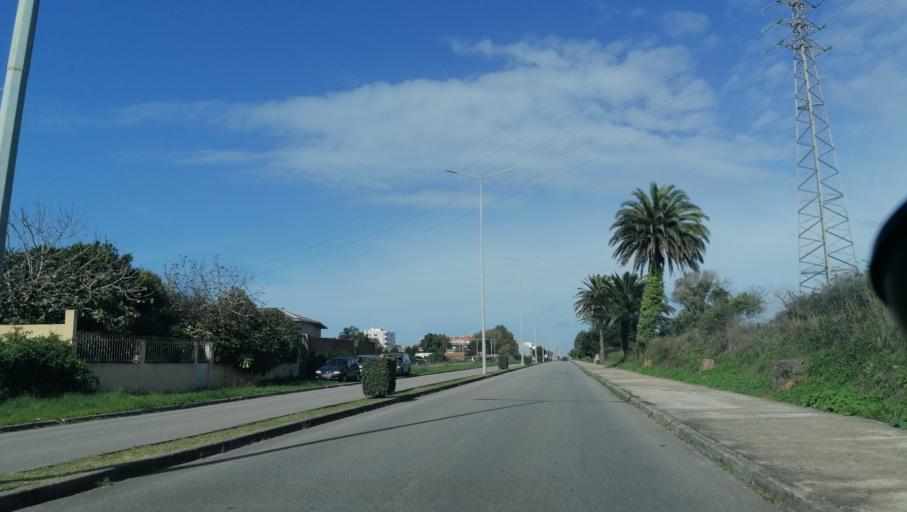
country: PT
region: Aveiro
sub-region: Espinho
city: Silvalde
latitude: 40.9995
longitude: -8.6343
